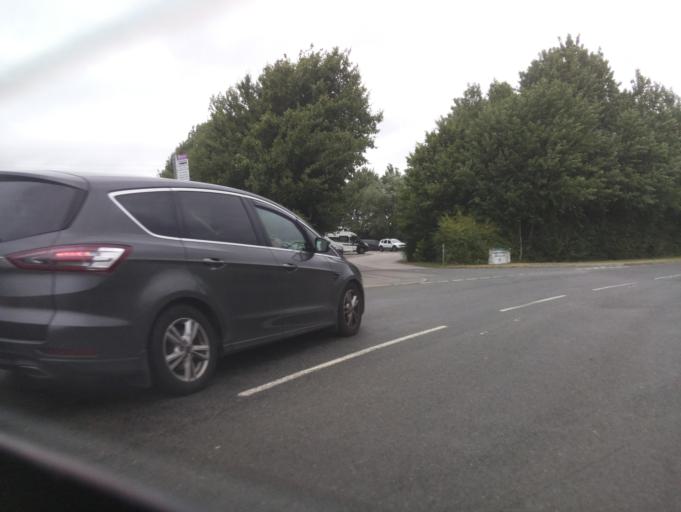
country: GB
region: England
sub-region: Derbyshire
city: Findern
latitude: 52.8588
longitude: -1.5553
